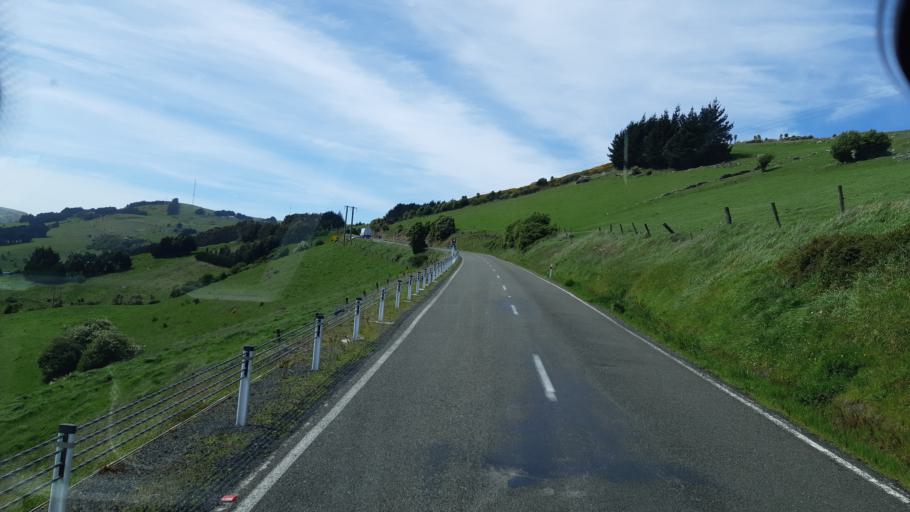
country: NZ
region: Otago
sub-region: Dunedin City
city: Dunedin
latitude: -45.8848
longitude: 170.5616
